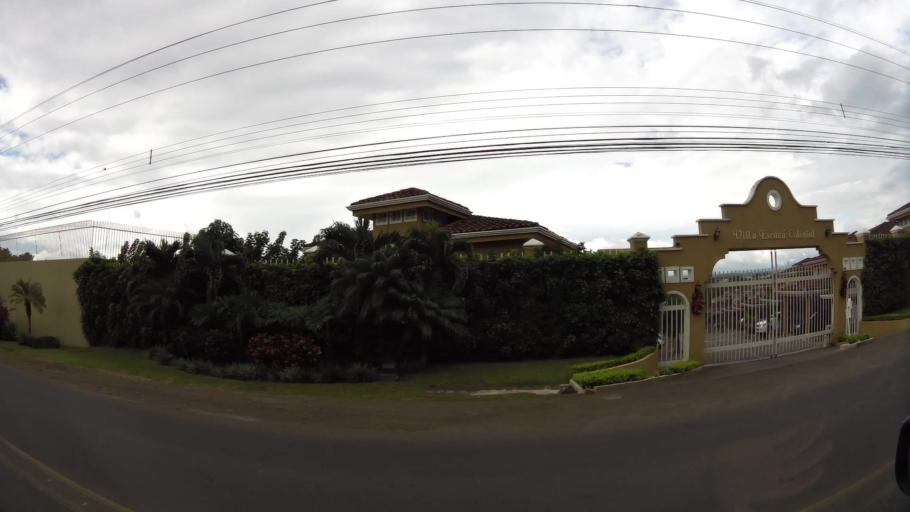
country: CR
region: Heredia
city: La Asuncion
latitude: 9.9576
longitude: -84.1699
